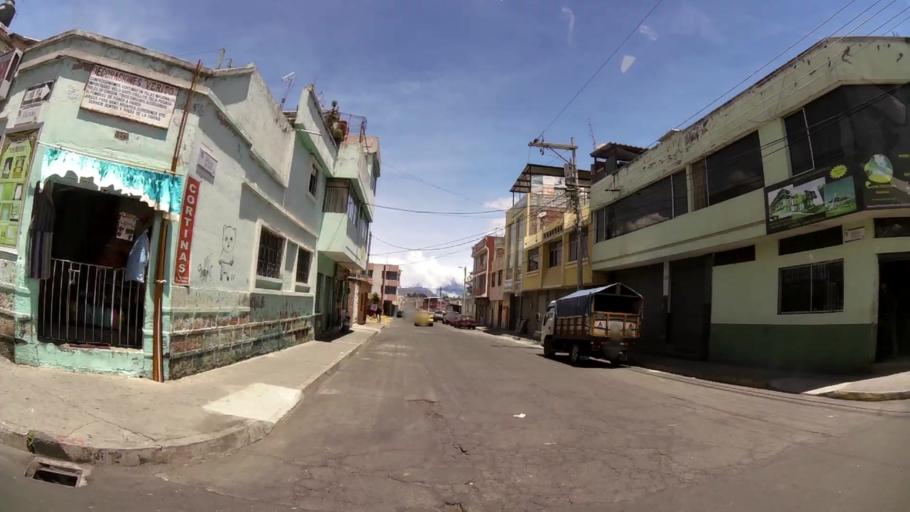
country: EC
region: Chimborazo
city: Riobamba
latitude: -1.6719
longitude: -78.6441
